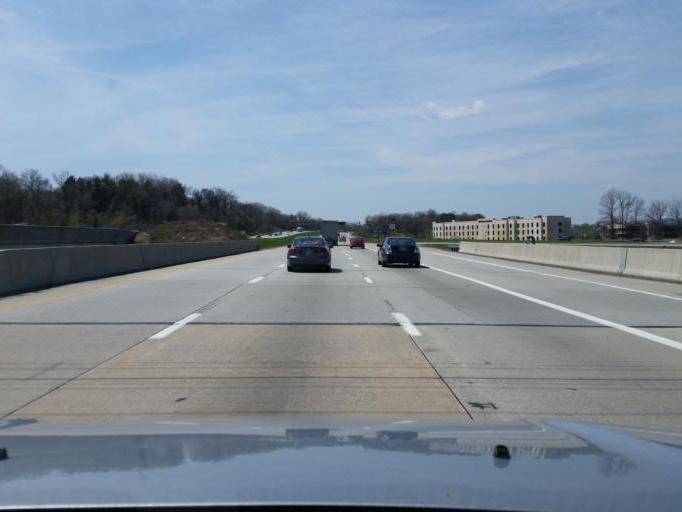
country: US
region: Pennsylvania
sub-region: Dauphin County
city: Progress
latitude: 40.3040
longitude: -76.8492
